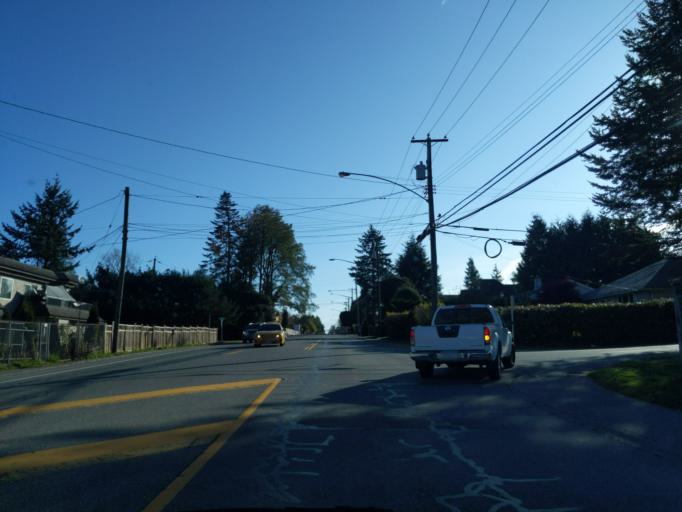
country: CA
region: British Columbia
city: New Westminster
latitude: 49.2030
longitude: -122.8562
